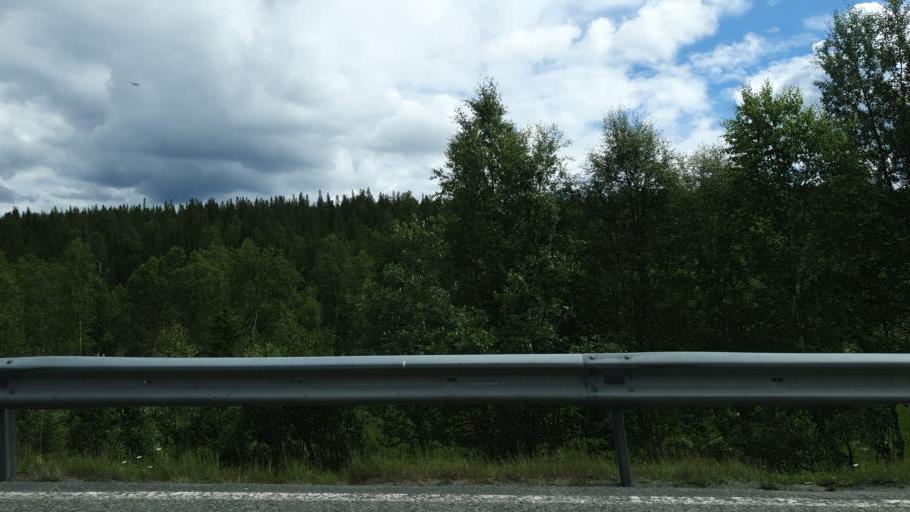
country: NO
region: Sor-Trondelag
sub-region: Rennebu
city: Berkak
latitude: 62.8558
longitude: 10.0213
